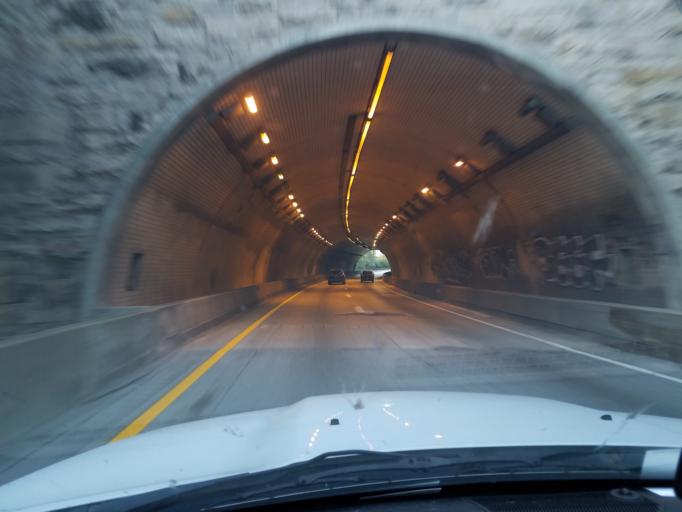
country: US
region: Kentucky
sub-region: Jefferson County
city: Saint Matthews
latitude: 38.2428
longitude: -85.6949
